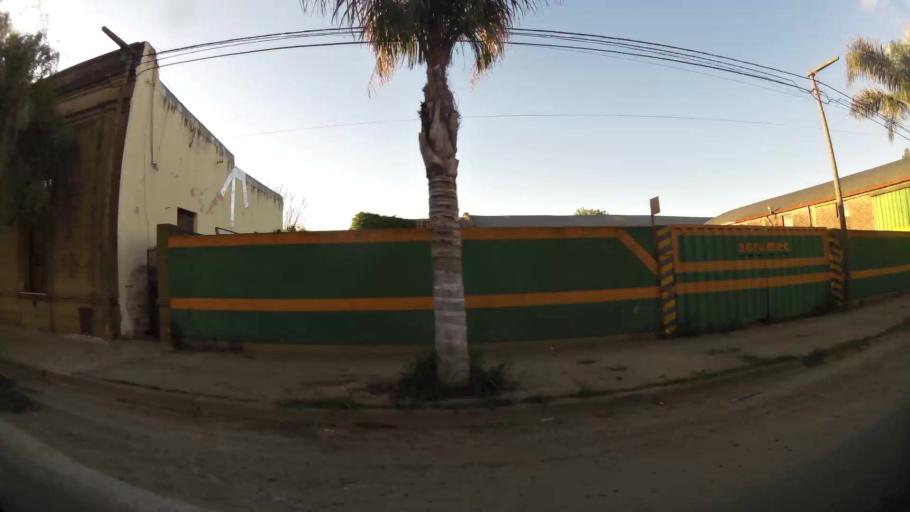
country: AR
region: Cordoba
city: Pozo del Molle
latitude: -32.0208
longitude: -62.9216
